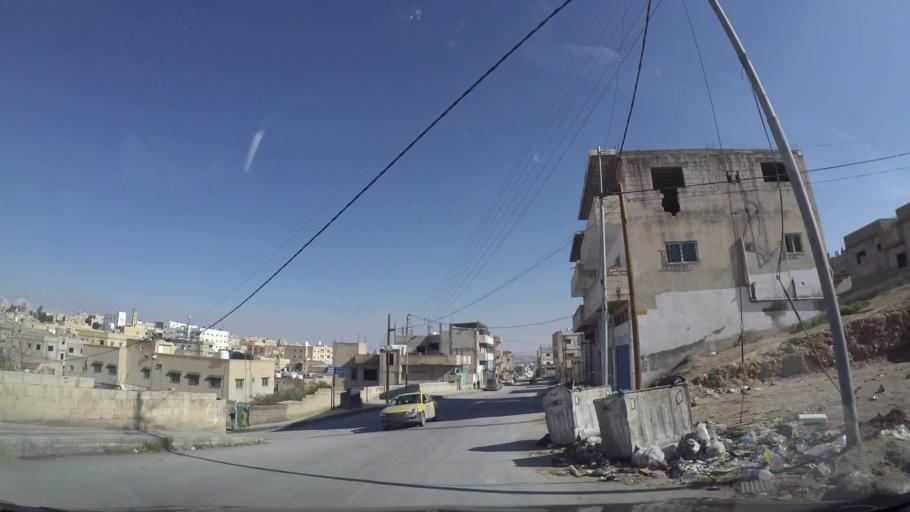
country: JO
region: Zarqa
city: Russeifa
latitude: 32.0360
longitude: 36.0343
